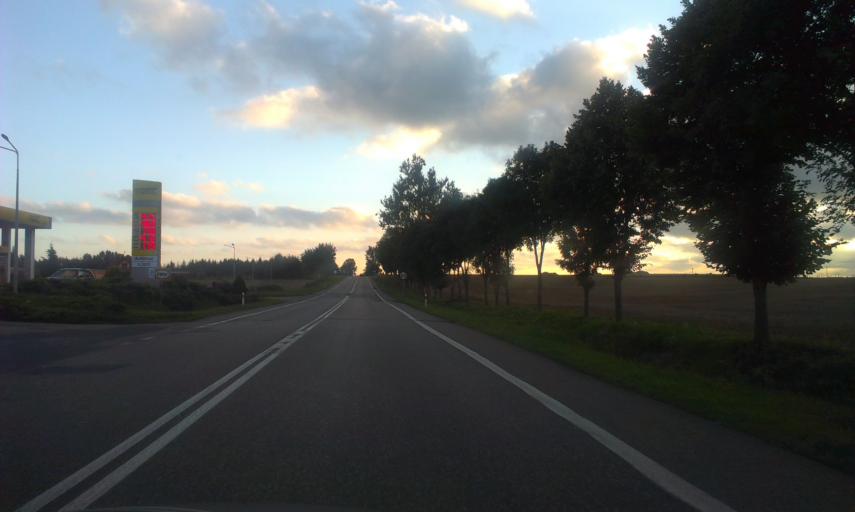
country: PL
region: West Pomeranian Voivodeship
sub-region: Powiat koszalinski
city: Sianow
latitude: 54.2394
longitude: 16.3281
